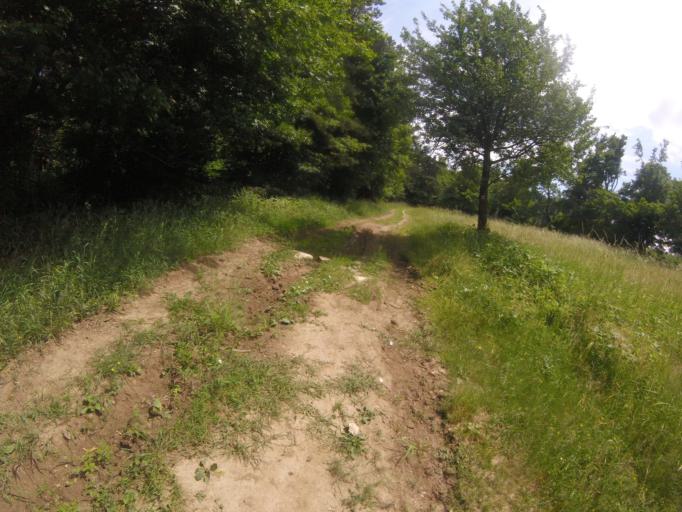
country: HU
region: Fejer
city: Szarliget
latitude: 47.5029
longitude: 18.4347
